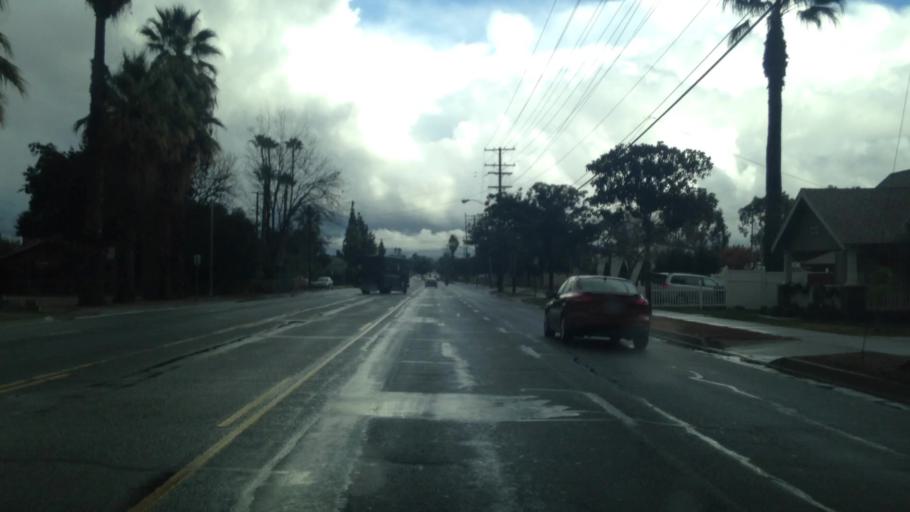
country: US
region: California
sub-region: Riverside County
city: Riverside
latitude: 33.9460
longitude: -117.4298
